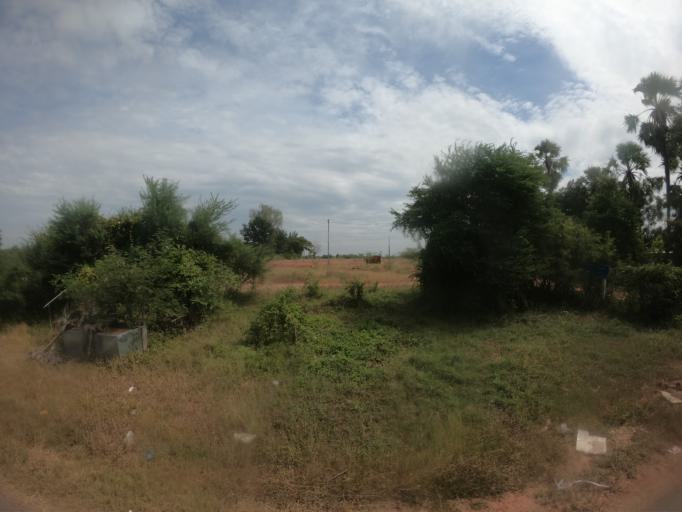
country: TH
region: Maha Sarakham
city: Chiang Yuen
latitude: 16.3879
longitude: 103.1020
